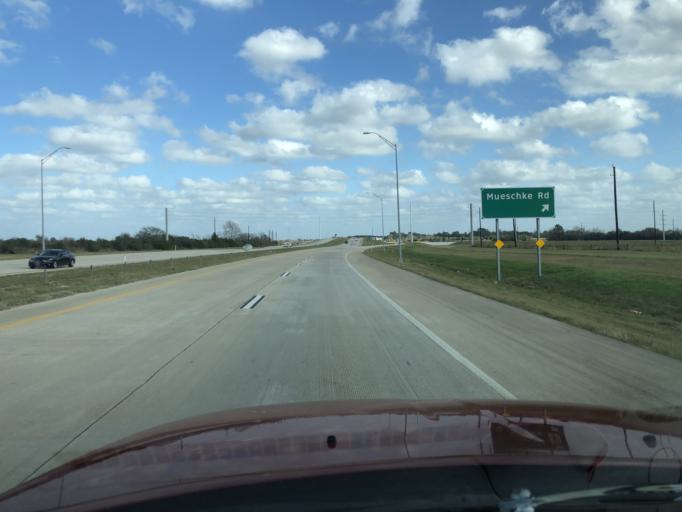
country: US
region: Texas
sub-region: Harris County
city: Cypress
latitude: 30.0531
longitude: -95.7410
